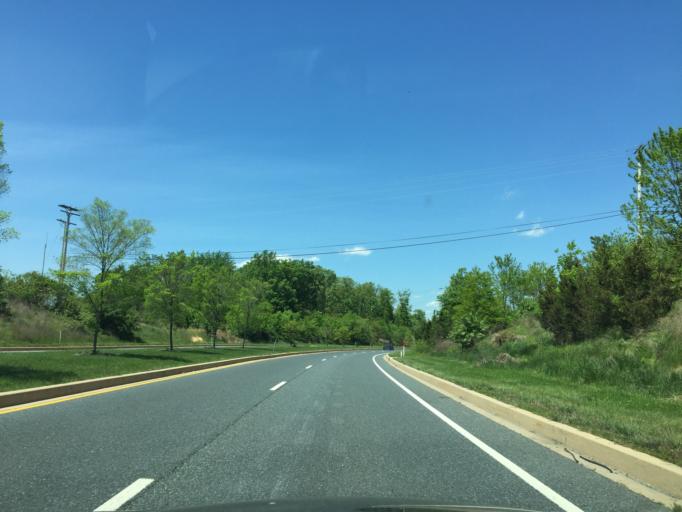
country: US
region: Maryland
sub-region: Baltimore County
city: White Marsh
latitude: 39.3651
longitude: -76.4262
